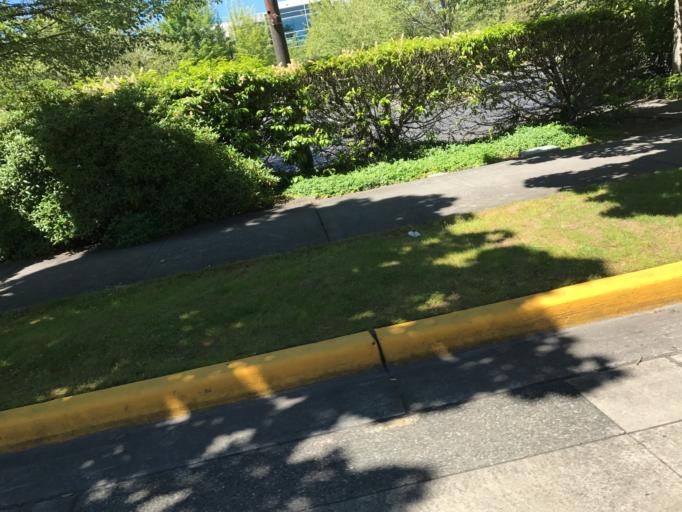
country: US
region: Washington
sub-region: King County
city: Redmond
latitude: 47.6366
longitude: -122.1292
